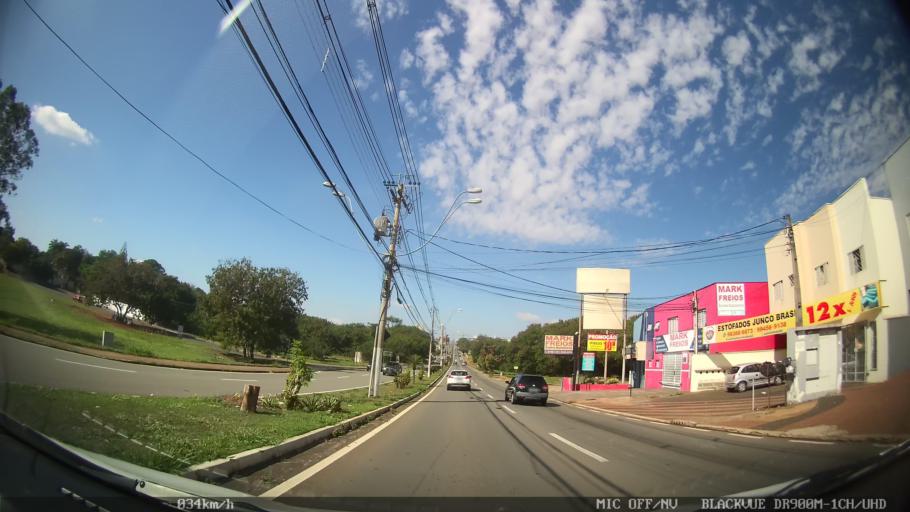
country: BR
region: Sao Paulo
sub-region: Americana
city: Americana
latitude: -22.7448
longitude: -47.3074
